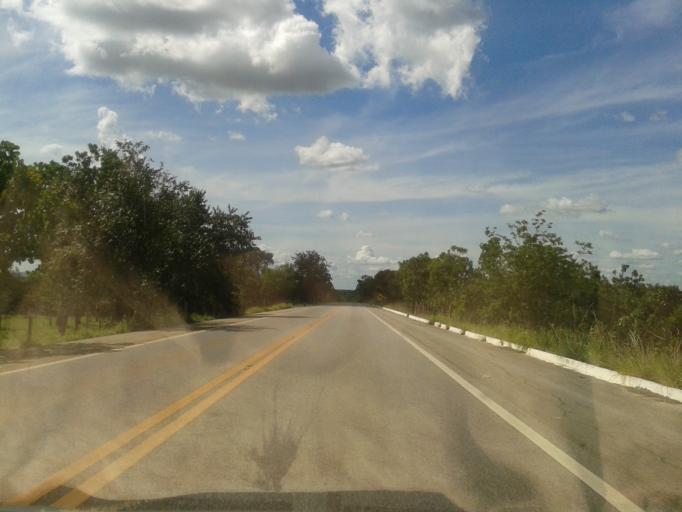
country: BR
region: Goias
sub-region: Itapuranga
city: Itapuranga
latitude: -15.4918
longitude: -50.3209
